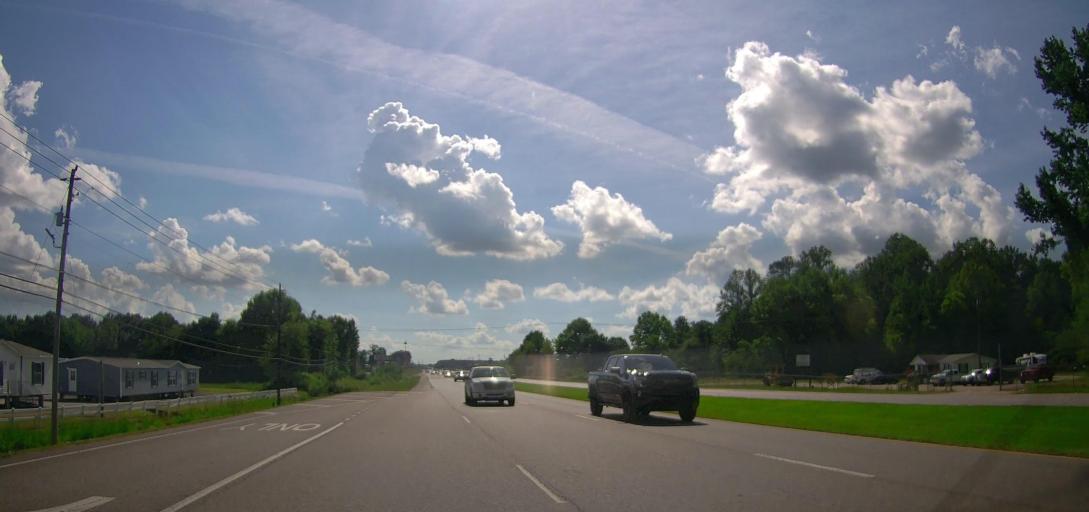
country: US
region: Alabama
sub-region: Tuscaloosa County
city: Northport
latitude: 33.2377
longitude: -87.6016
